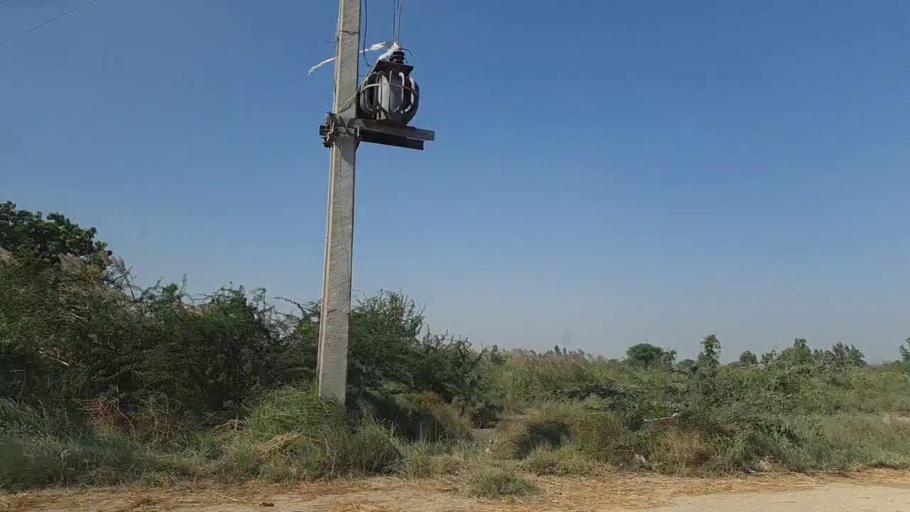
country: PK
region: Sindh
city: Daro Mehar
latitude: 24.7914
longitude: 68.1726
